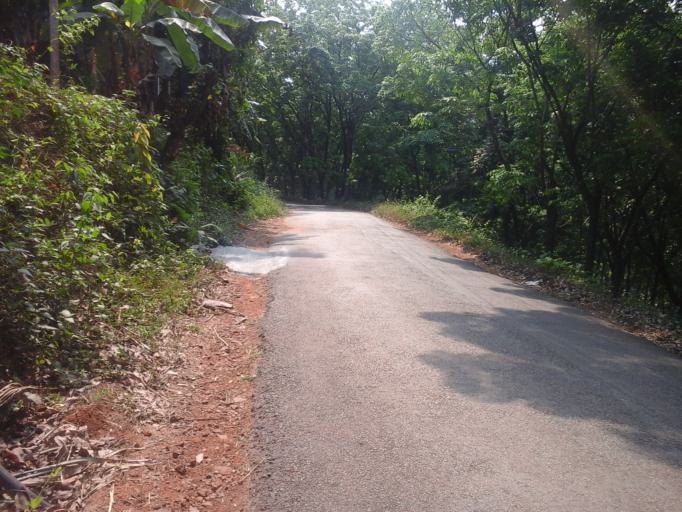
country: IN
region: Kerala
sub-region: Kannur
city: Taliparamba
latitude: 12.1491
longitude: 75.4341
